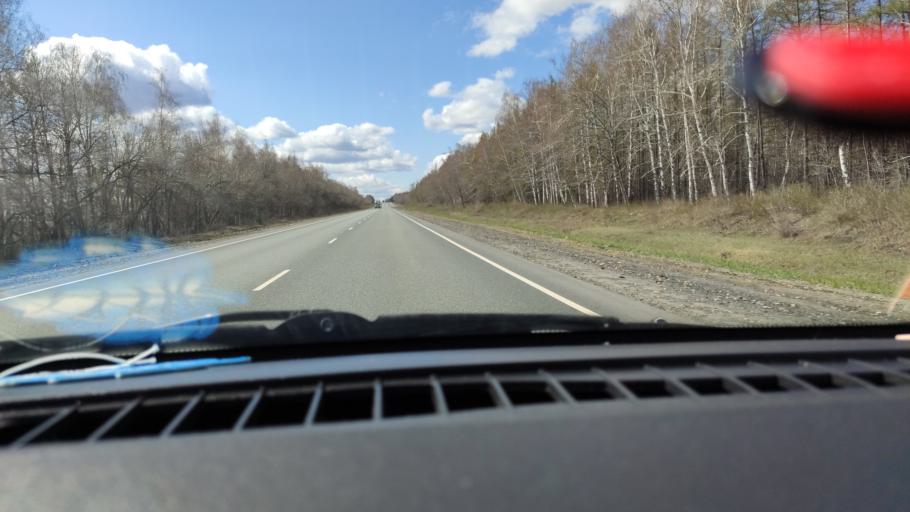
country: RU
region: Saratov
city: Khvalynsk
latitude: 52.5670
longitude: 48.0969
